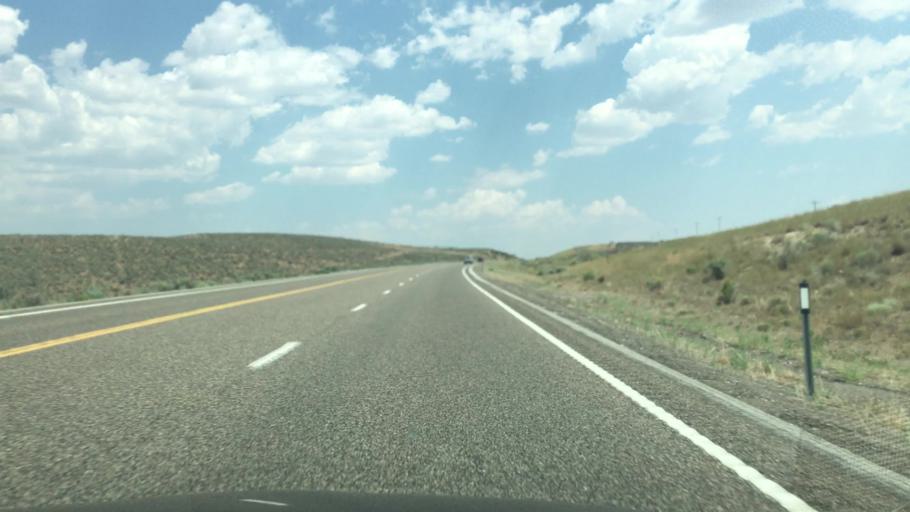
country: US
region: Nevada
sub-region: Elko County
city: Wells
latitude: 41.1863
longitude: -114.8737
